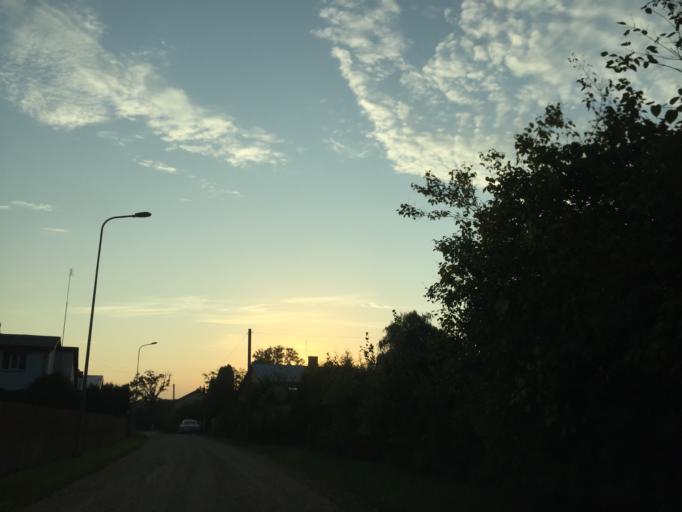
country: LV
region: Baldone
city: Baldone
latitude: 56.7478
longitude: 24.3944
